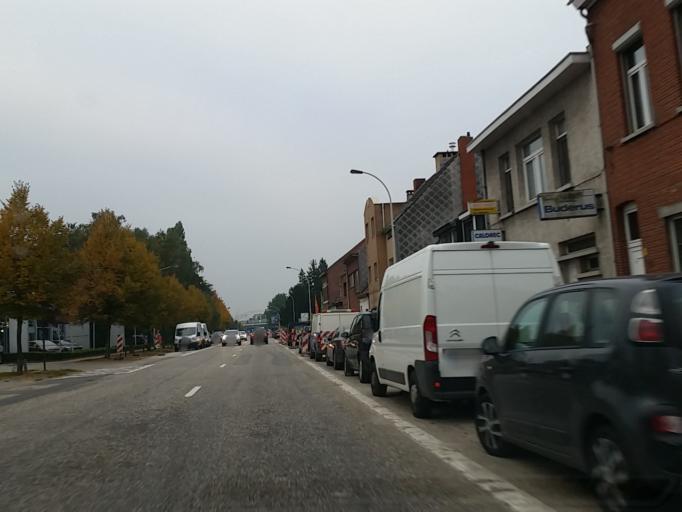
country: BE
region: Flanders
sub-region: Provincie Antwerpen
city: Brasschaat
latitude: 51.2741
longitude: 4.4568
